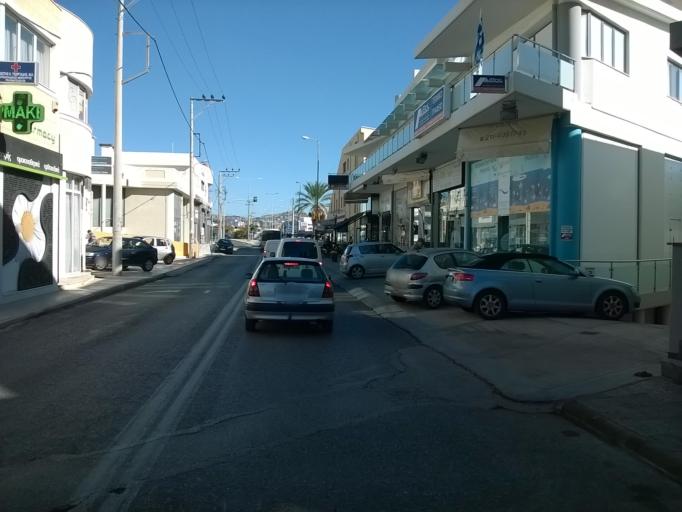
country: GR
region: Attica
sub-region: Nomarchia Anatolikis Attikis
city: Vari
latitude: 37.8335
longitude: 23.8033
